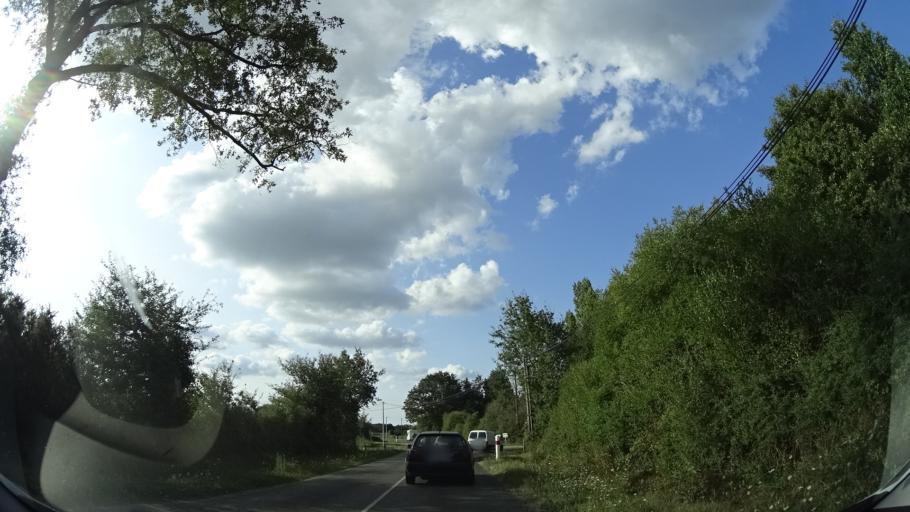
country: FR
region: Pays de la Loire
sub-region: Departement de la Loire-Atlantique
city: Casson
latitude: 47.3992
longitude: -1.5281
